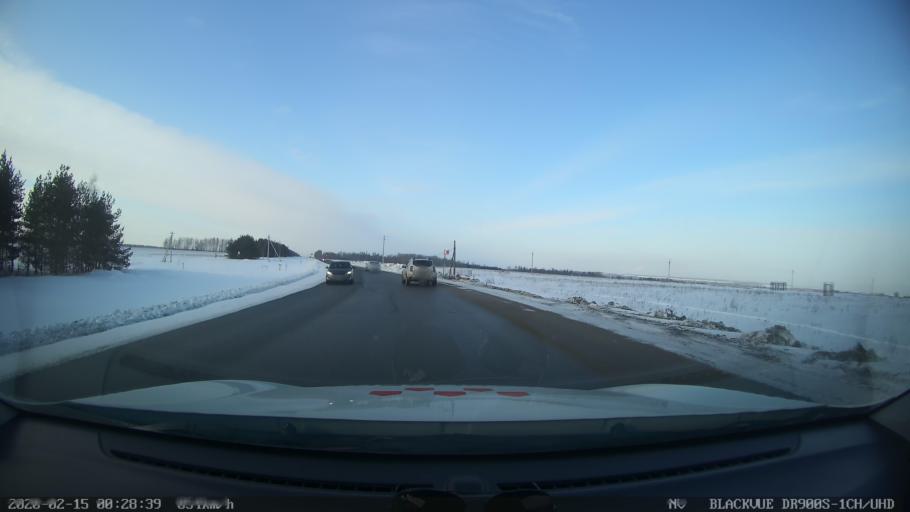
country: RU
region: Tatarstan
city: Verkhniy Uslon
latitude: 55.6441
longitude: 48.8754
